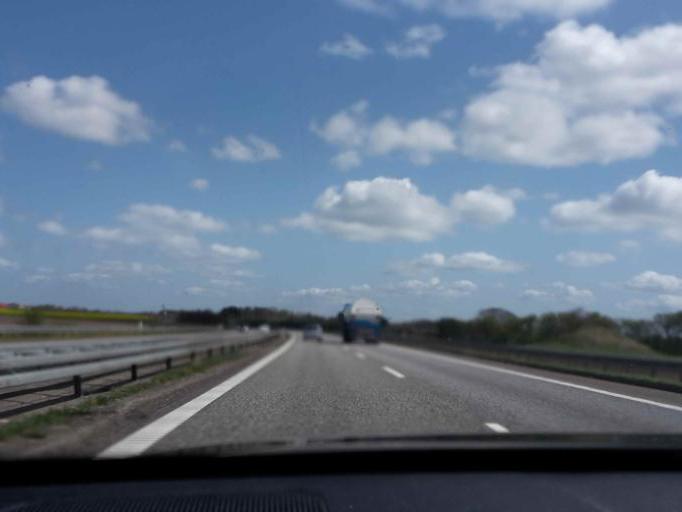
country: DK
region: South Denmark
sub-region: Kolding Kommune
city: Lunderskov
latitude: 55.4977
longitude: 9.2200
